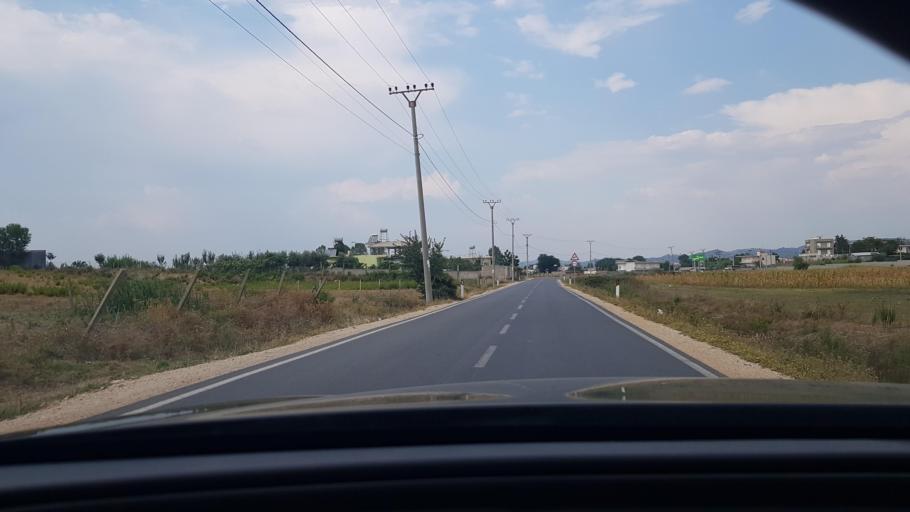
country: AL
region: Durres
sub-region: Rrethi i Durresit
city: Katundi i Ri
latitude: 41.4183
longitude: 19.5469
